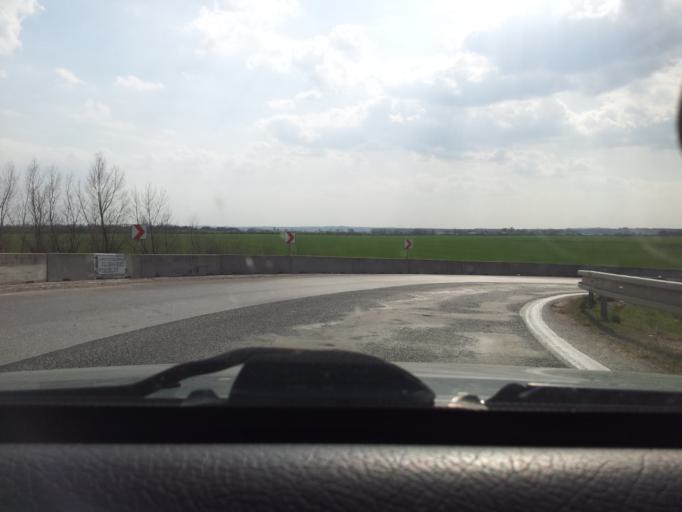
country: SK
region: Nitriansky
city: Tlmace
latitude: 48.2039
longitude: 18.5103
